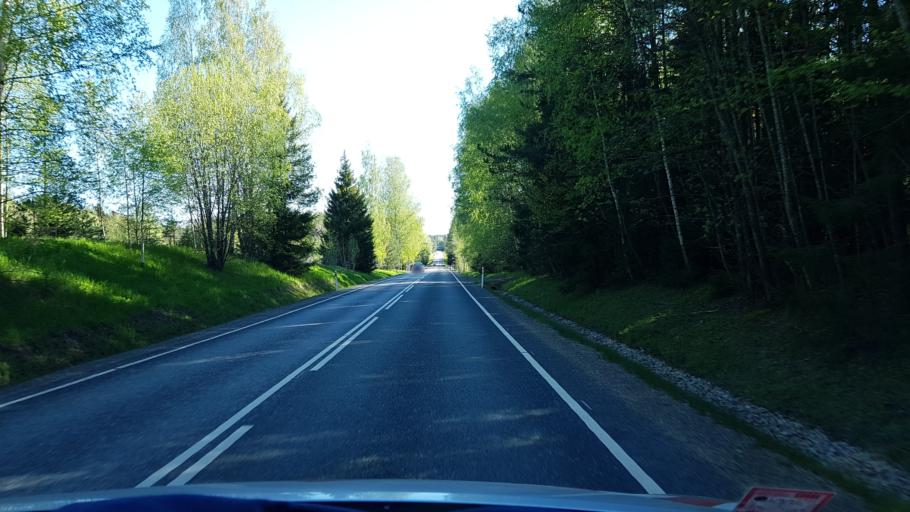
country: EE
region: Polvamaa
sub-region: Polva linn
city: Polva
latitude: 58.1182
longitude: 27.1335
